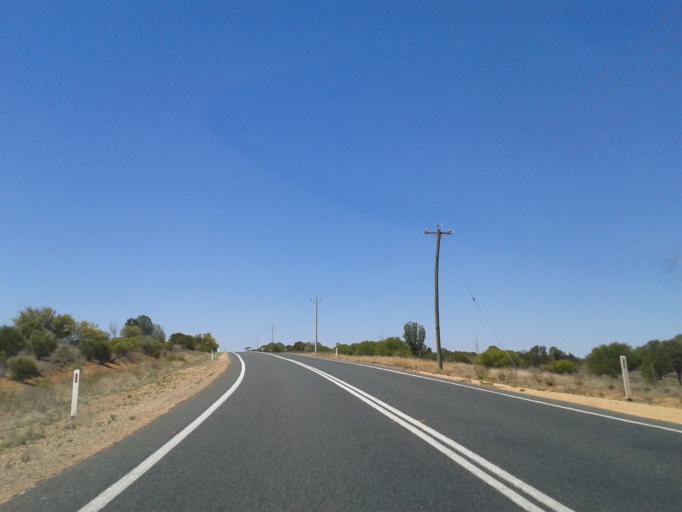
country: AU
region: New South Wales
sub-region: Wentworth
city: Gol Gol
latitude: -34.2633
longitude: 142.2555
